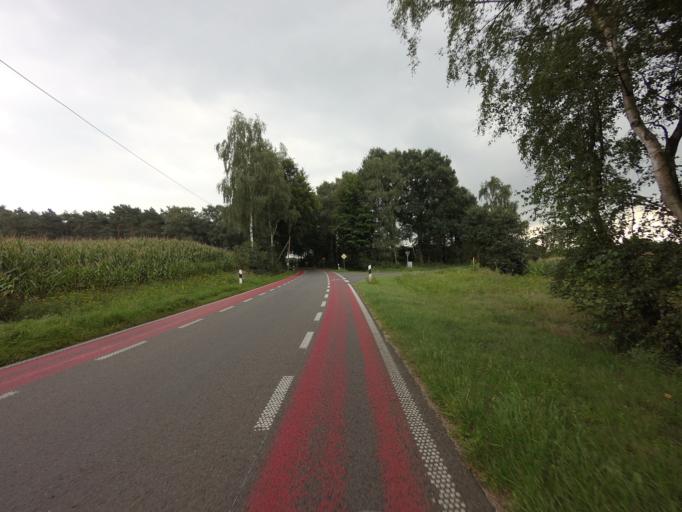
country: DE
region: Lower Saxony
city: Getelo
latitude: 52.4573
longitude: 6.8624
